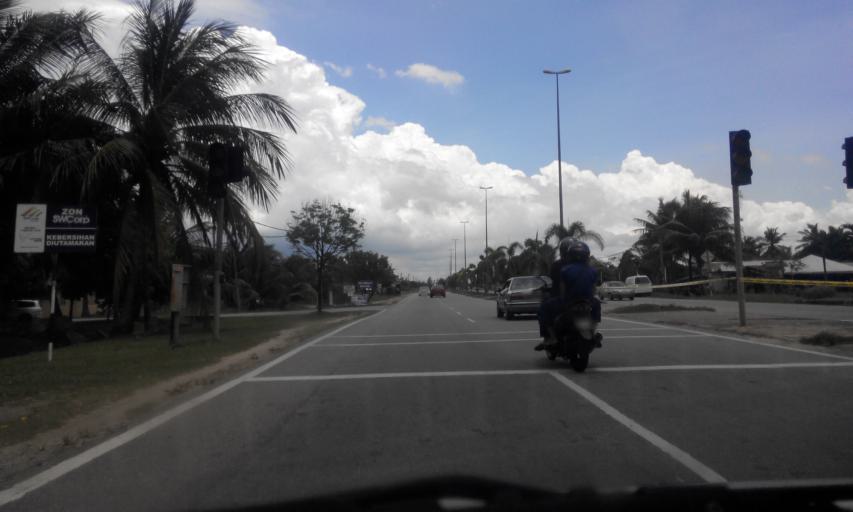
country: MY
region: Perak
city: Parit Buntar
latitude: 5.1308
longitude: 100.4989
